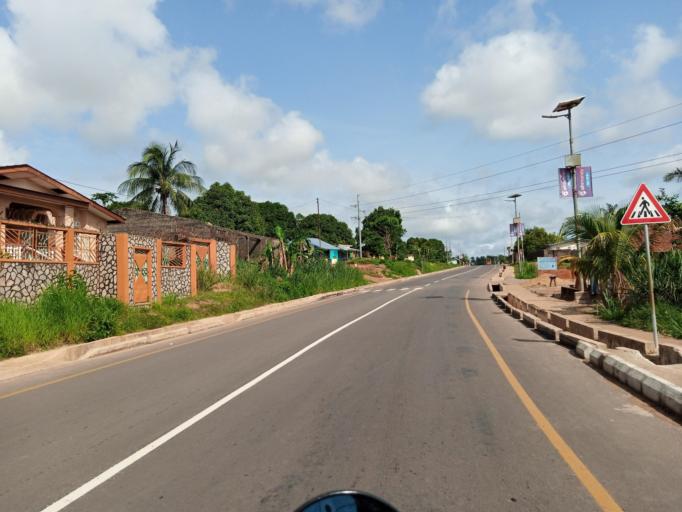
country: SL
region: Southern Province
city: Bo
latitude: 7.9496
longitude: -11.7141
